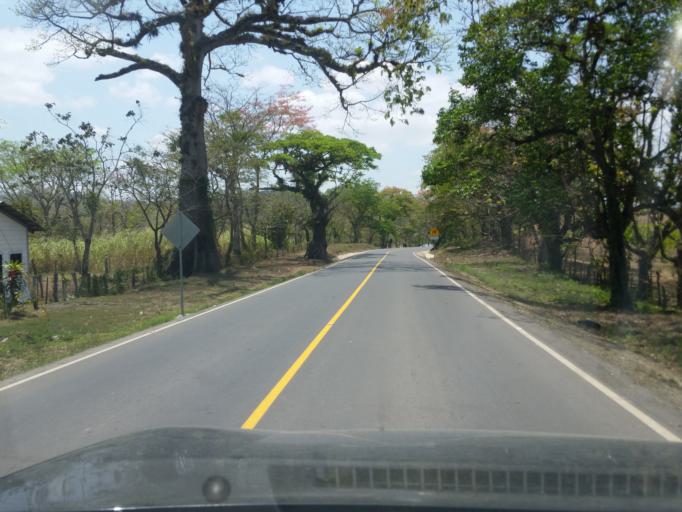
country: NI
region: Boaco
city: Boaco
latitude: 12.5735
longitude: -85.5414
